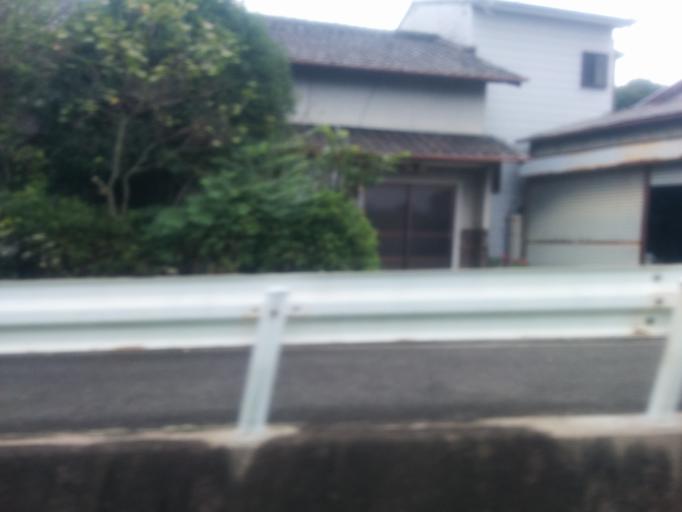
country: JP
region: Kyoto
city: Uji
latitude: 34.9464
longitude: 135.7748
